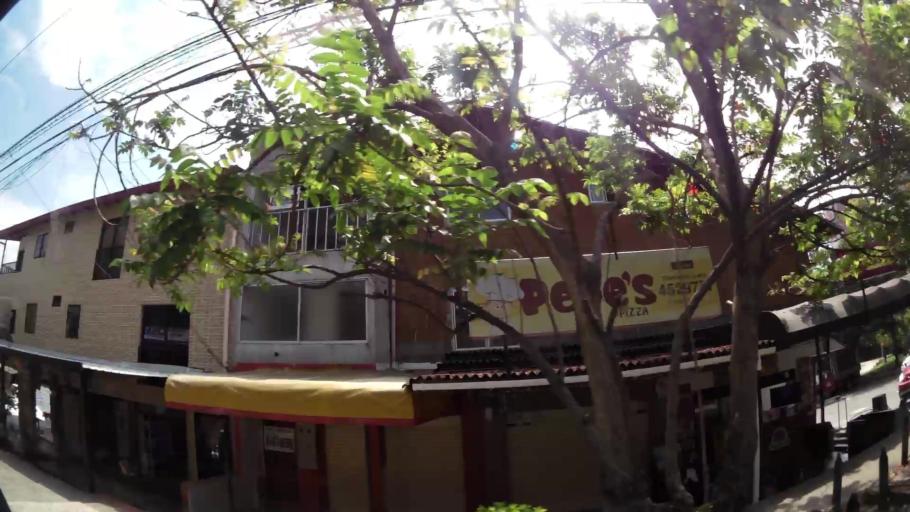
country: CO
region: Antioquia
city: Bello
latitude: 6.3194
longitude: -75.5594
